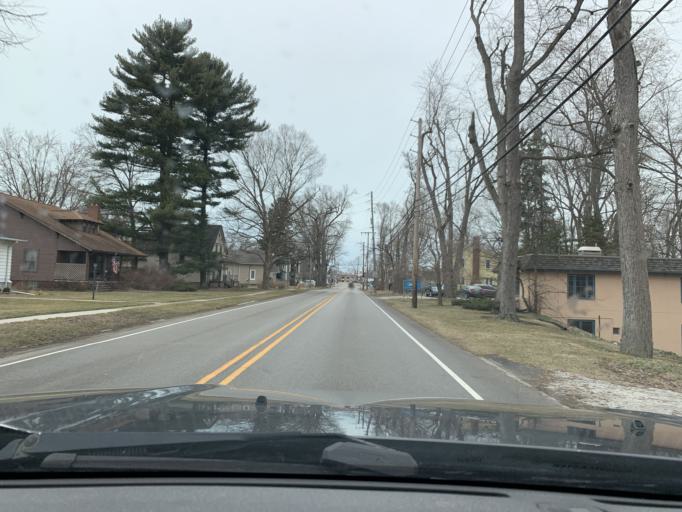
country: US
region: Indiana
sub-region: Porter County
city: Chesterton
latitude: 41.6049
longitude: -87.0515
